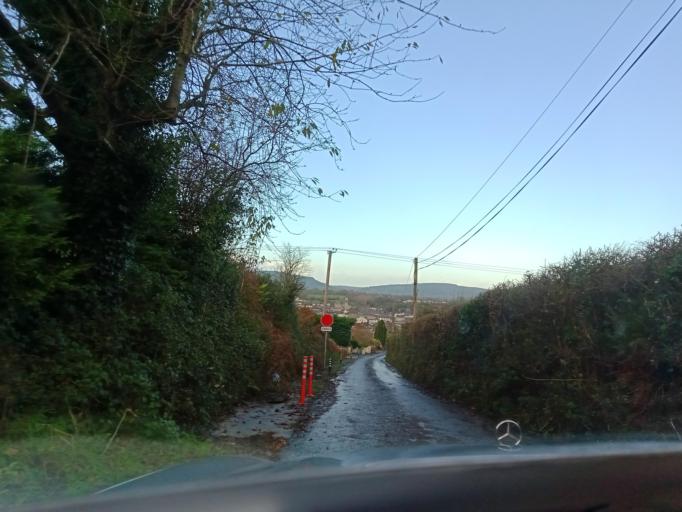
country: IE
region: Munster
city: Carrick-on-Suir
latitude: 52.3389
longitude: -7.4142
